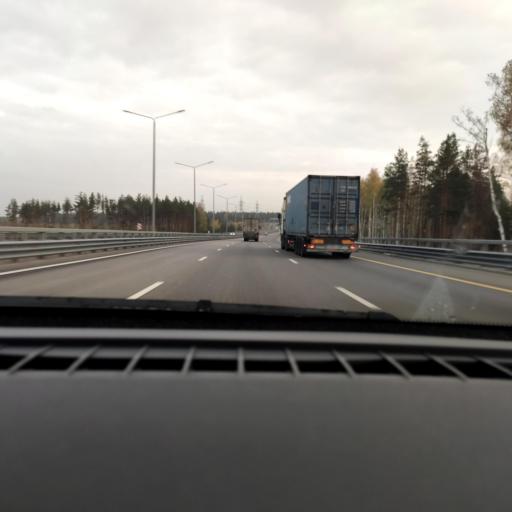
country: RU
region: Voronezj
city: Somovo
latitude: 51.7331
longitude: 39.3103
